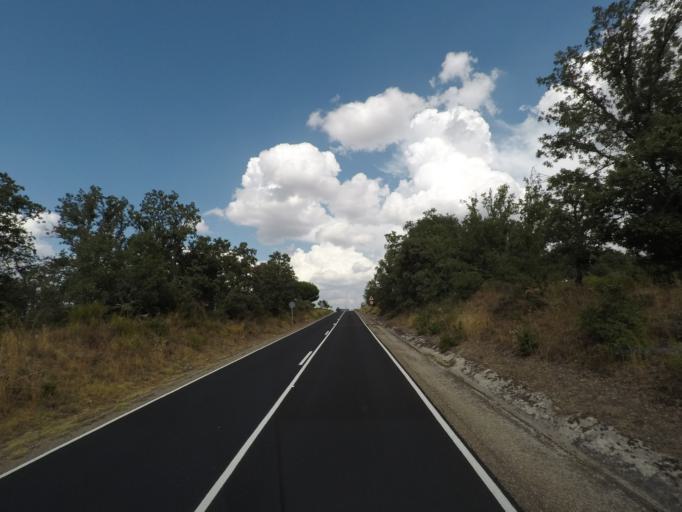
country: ES
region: Castille and Leon
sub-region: Provincia de Zamora
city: Fermoselle
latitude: 41.3132
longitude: -6.3088
